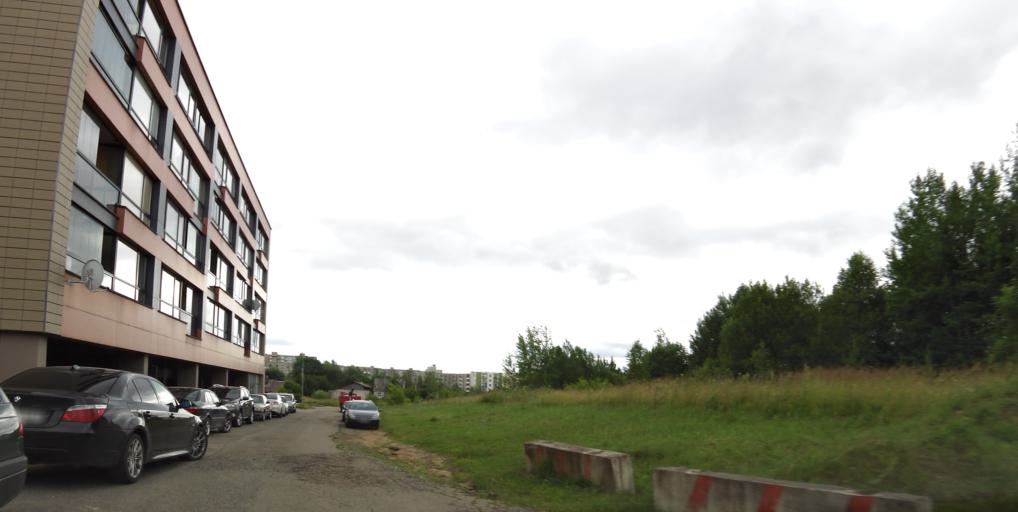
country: LT
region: Vilnius County
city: Pilaite
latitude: 54.7125
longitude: 25.1783
